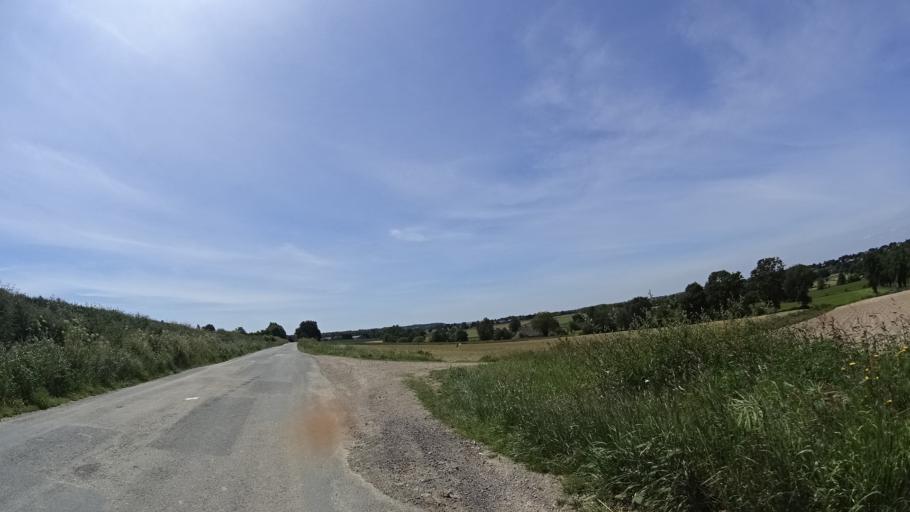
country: FR
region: Brittany
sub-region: Departement d'Ille-et-Vilaine
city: Iffendic
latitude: 48.1327
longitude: -1.9957
